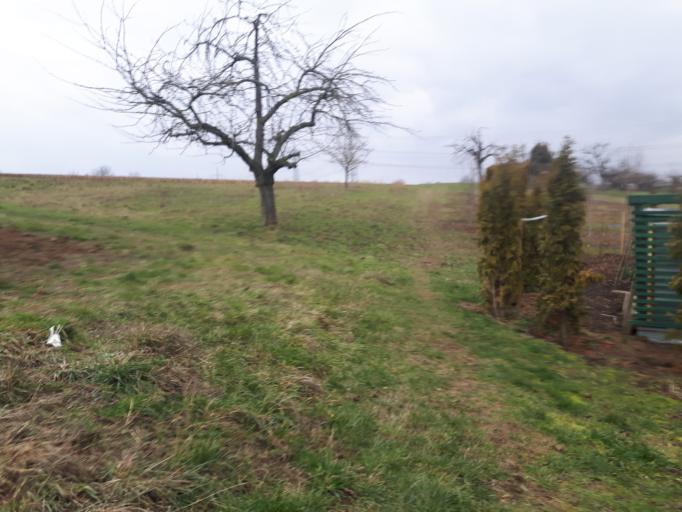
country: DE
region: Baden-Wuerttemberg
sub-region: Regierungsbezirk Stuttgart
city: Nordheim
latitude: 49.1120
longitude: 9.1482
